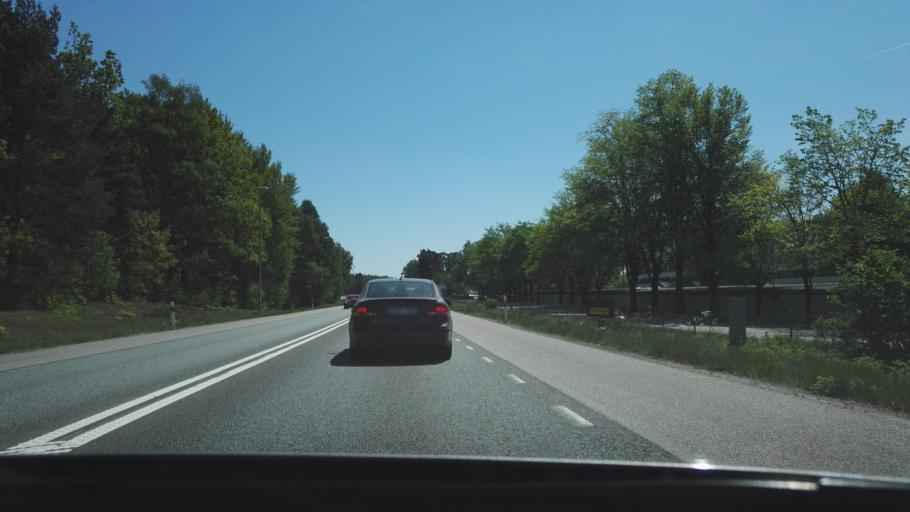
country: SE
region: Kronoberg
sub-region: Vaxjo Kommun
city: Vaexjoe
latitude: 56.8855
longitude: 14.8288
